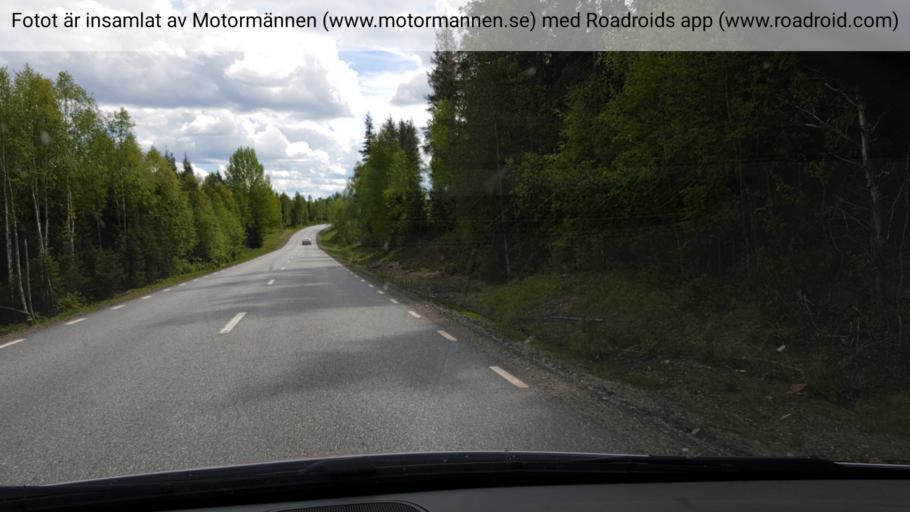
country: SE
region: Vaesterbotten
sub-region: Umea Kommun
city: Ersmark
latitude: 64.3198
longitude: 20.2238
